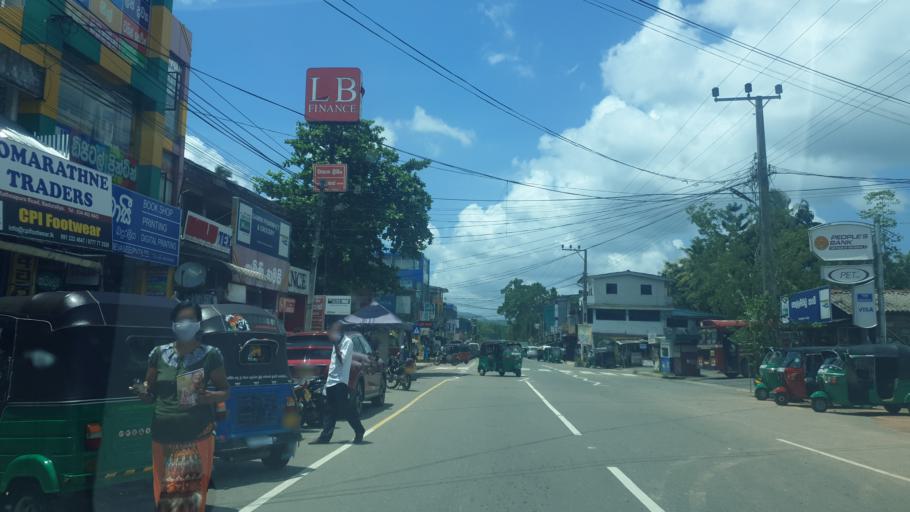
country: LK
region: Western
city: Horawala Junction
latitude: 6.5169
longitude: 80.2318
